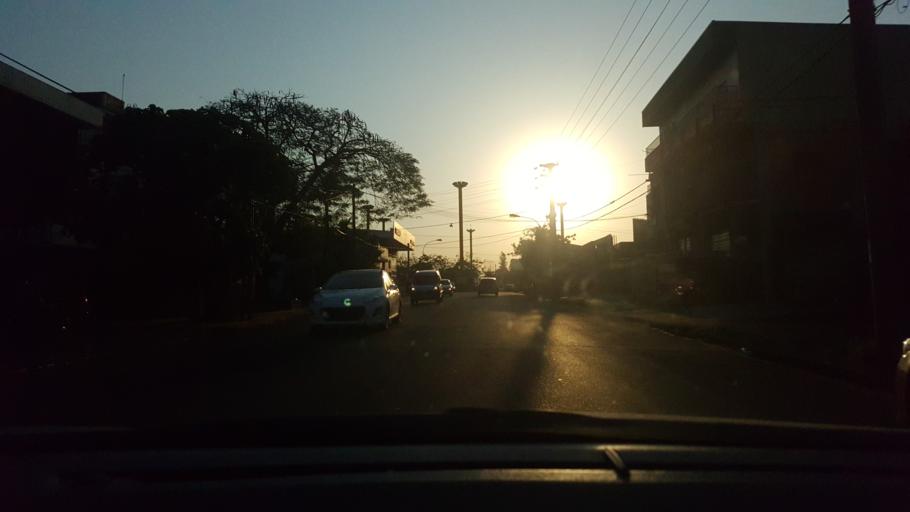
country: AR
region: Misiones
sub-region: Departamento de Capital
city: Posadas
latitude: -27.4047
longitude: -55.9010
